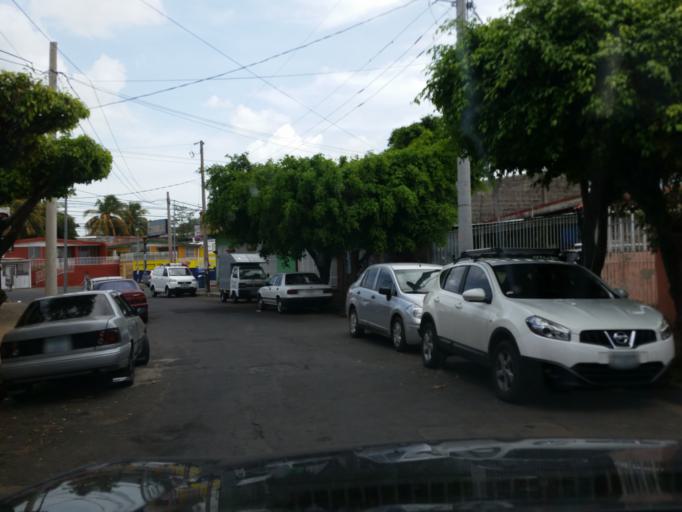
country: NI
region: Managua
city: Managua
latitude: 12.1254
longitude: -86.2532
